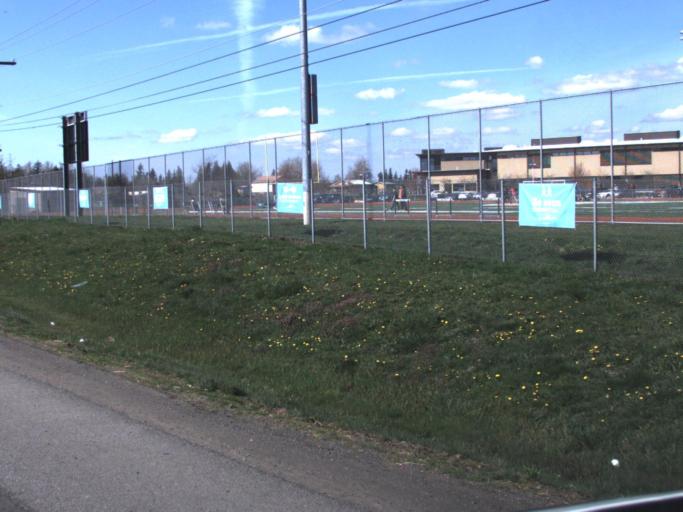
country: US
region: Washington
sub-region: King County
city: Lea Hill
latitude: 47.2621
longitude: -122.1378
